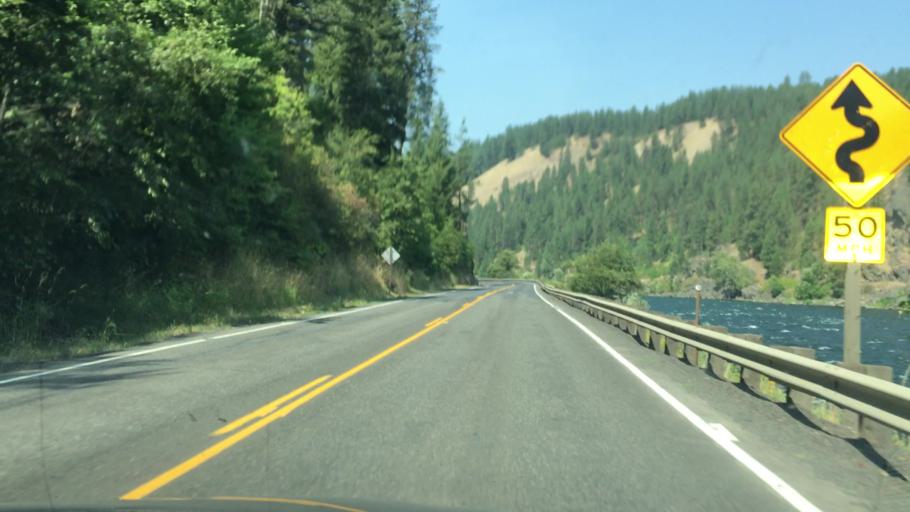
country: US
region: Idaho
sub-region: Clearwater County
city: Orofino
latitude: 46.4996
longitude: -116.3848
